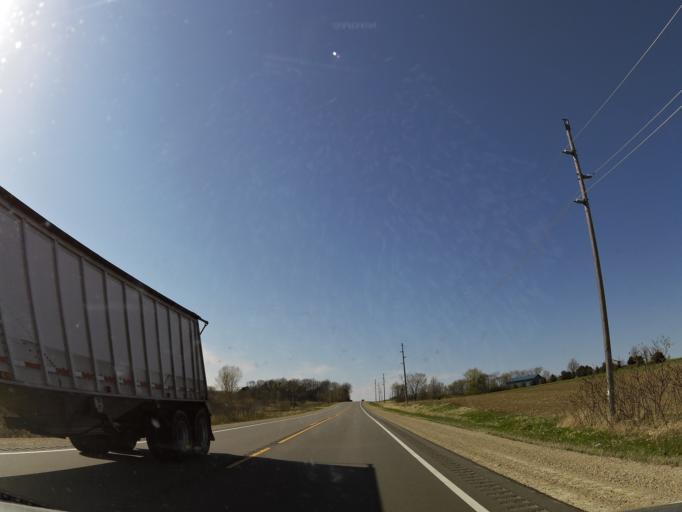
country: US
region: Wisconsin
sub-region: Pierce County
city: Ellsworth
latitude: 44.7005
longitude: -92.4096
